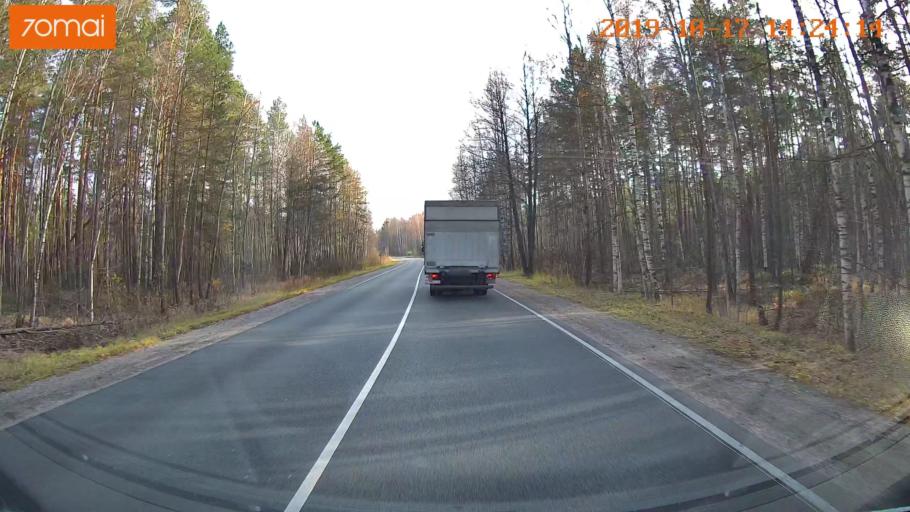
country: RU
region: Moskovskaya
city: Radovitskiy
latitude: 55.0110
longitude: 39.9660
